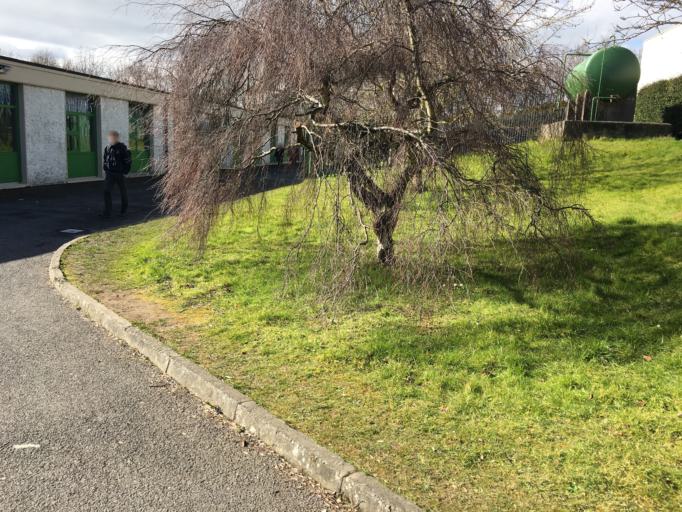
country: IE
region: Leinster
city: Portmarnock
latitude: 53.4321
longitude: -6.1375
